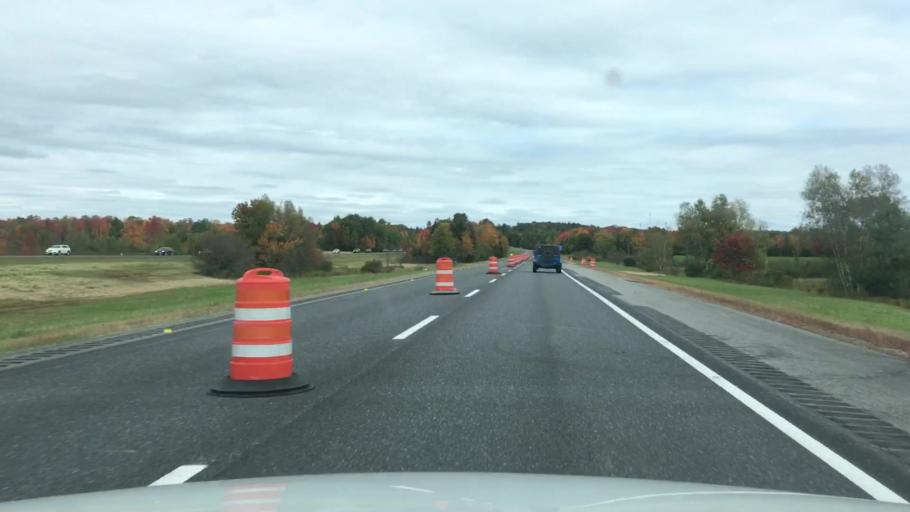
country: US
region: Maine
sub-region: Sagadahoc County
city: Richmond
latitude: 44.1521
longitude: -69.8379
